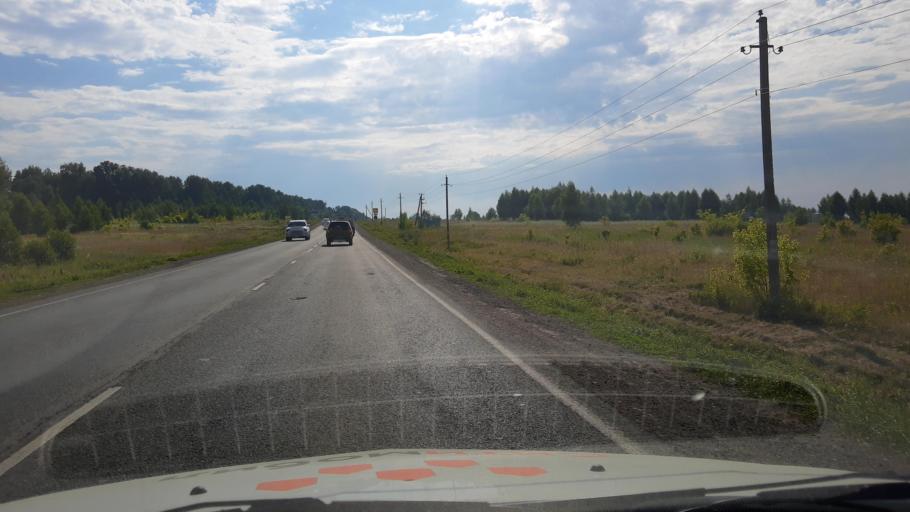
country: RU
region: Bashkortostan
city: Iglino
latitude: 54.8145
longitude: 56.3598
